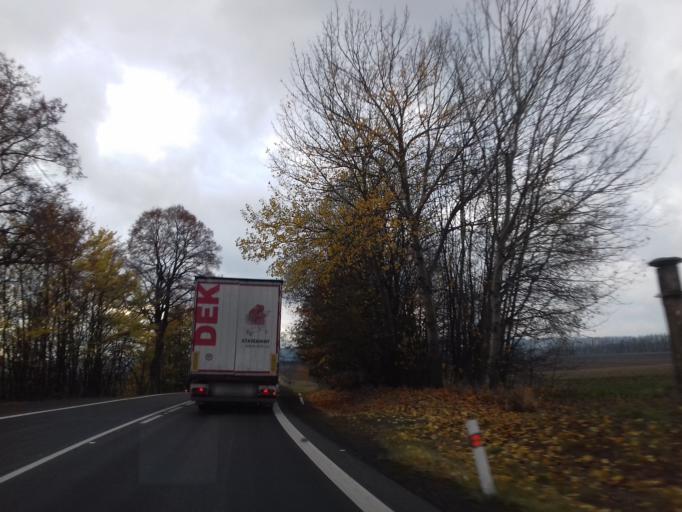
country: CZ
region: Pardubicky
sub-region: Okres Svitavy
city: Svitavy
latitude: 49.7599
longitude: 16.5078
